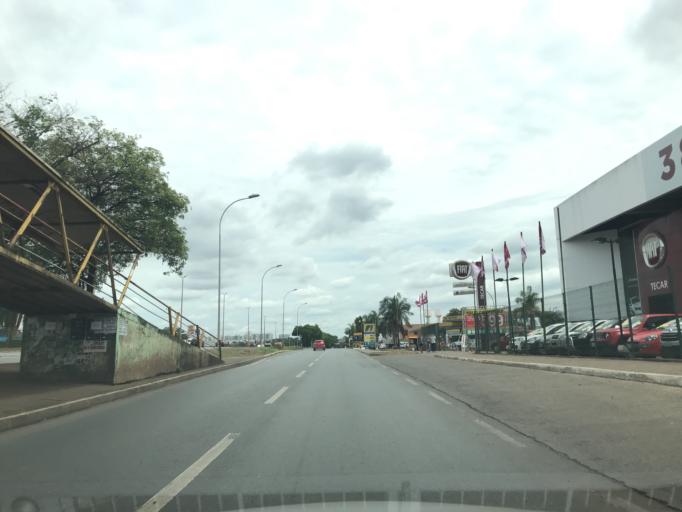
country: BR
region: Federal District
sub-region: Brasilia
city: Brasilia
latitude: -15.8529
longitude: -47.9549
